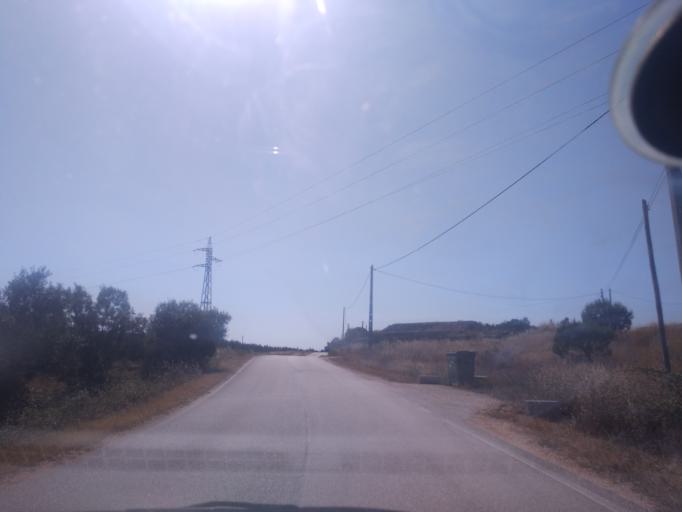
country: PT
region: Faro
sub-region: Aljezur
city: Aljezur
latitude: 37.2197
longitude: -8.7952
